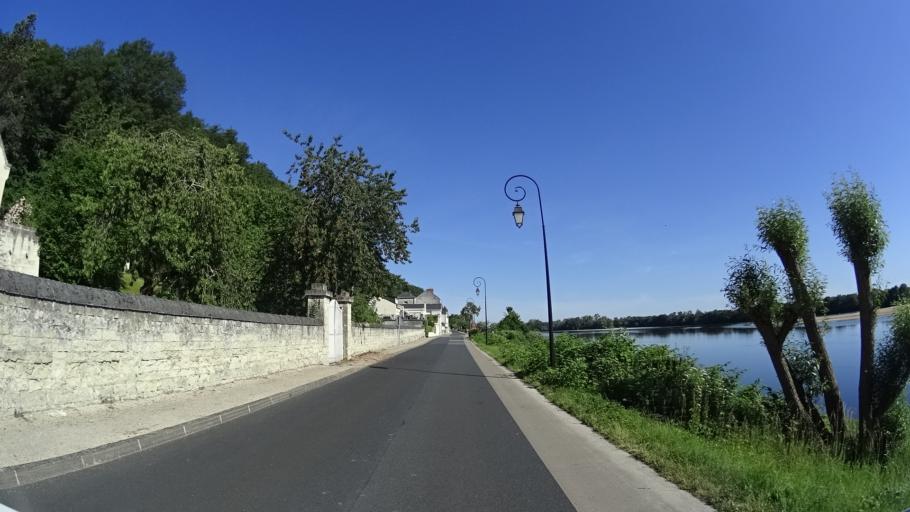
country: FR
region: Pays de la Loire
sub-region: Departement de Maine-et-Loire
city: Saint-Martin-de-la-Place
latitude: 47.2970
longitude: -0.1399
